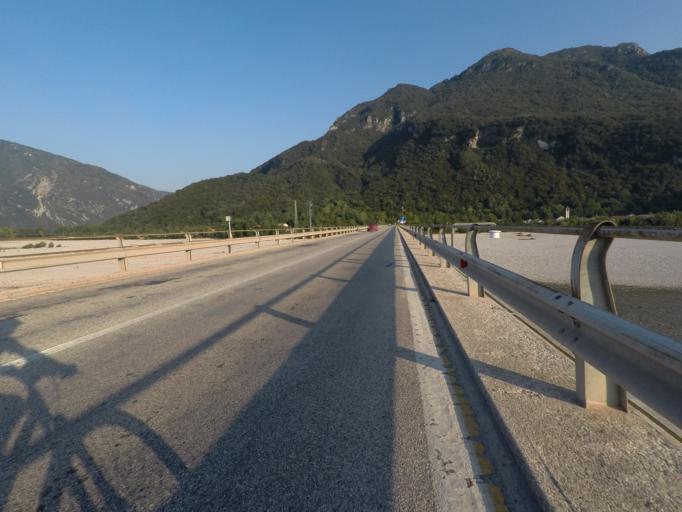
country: IT
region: Friuli Venezia Giulia
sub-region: Provincia di Udine
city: Trasaghis
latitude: 46.2817
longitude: 13.0951
